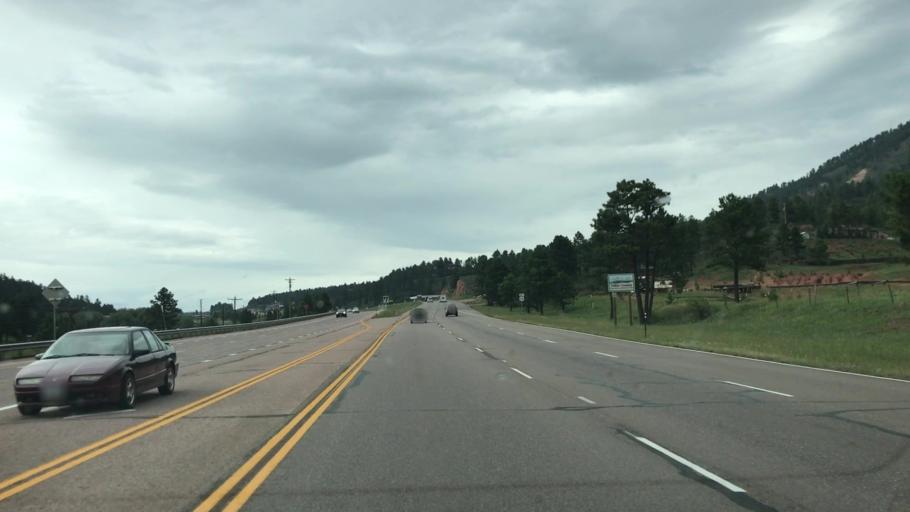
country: US
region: Colorado
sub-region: El Paso County
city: Cascade-Chipita Park
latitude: 38.9583
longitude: -105.0282
